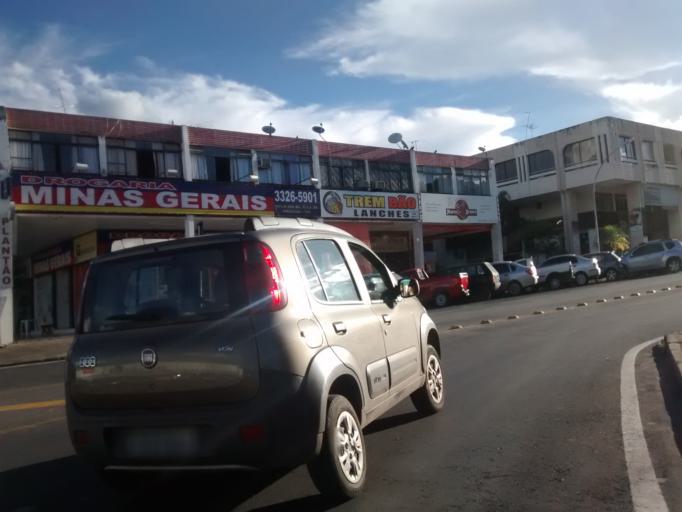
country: BR
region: Federal District
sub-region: Brasilia
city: Brasilia
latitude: -15.7731
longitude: -47.8756
